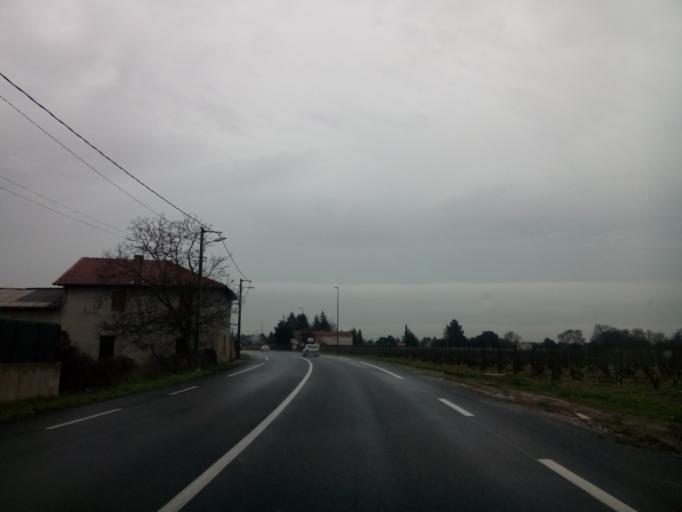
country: FR
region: Rhone-Alpes
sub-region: Departement de la Drome
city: Mercurol
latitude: 45.0691
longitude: 4.8717
